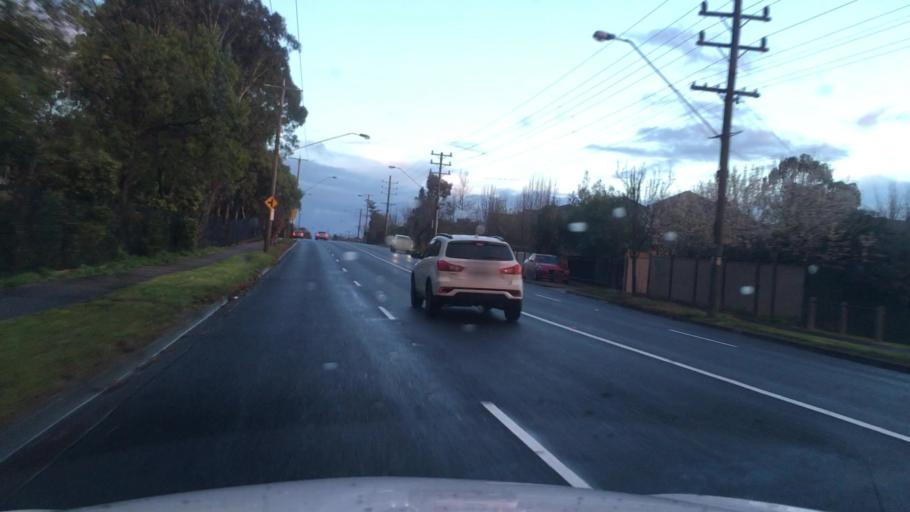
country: AU
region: Victoria
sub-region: Whitehorse
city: Surrey Hills
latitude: -37.8395
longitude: 145.0976
